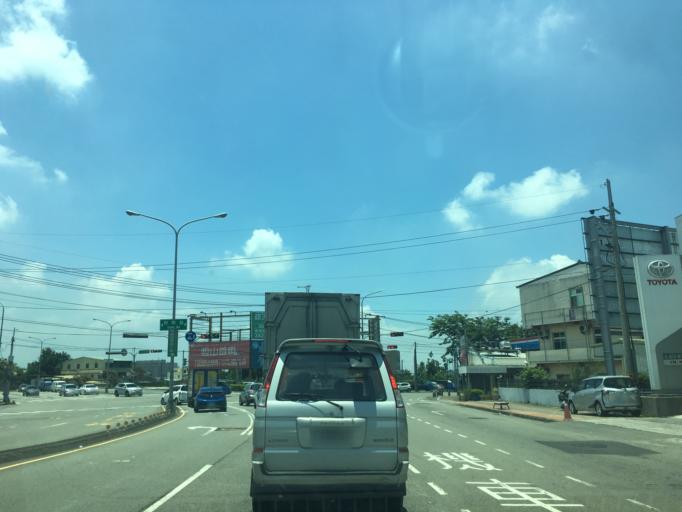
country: TW
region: Taiwan
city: Fengyuan
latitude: 24.2390
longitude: 120.7031
